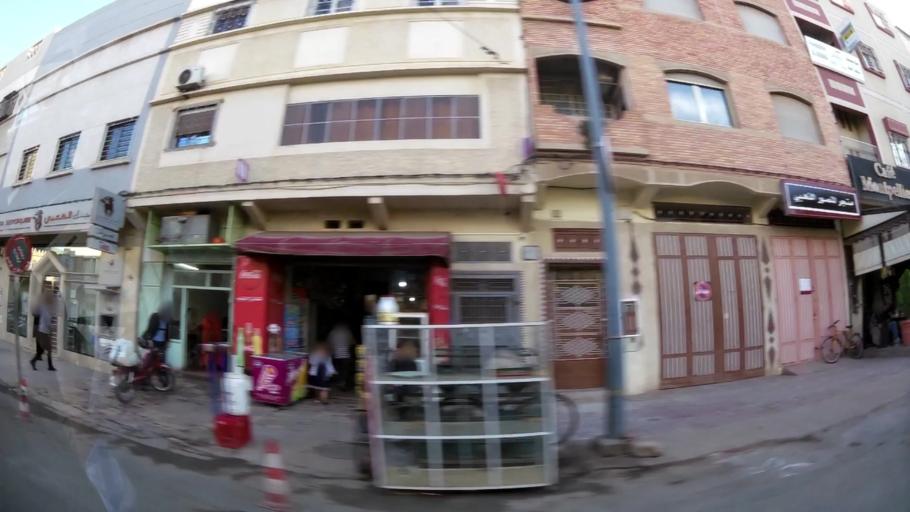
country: MA
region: Oriental
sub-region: Oujda-Angad
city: Oujda
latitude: 34.7022
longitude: -1.9132
